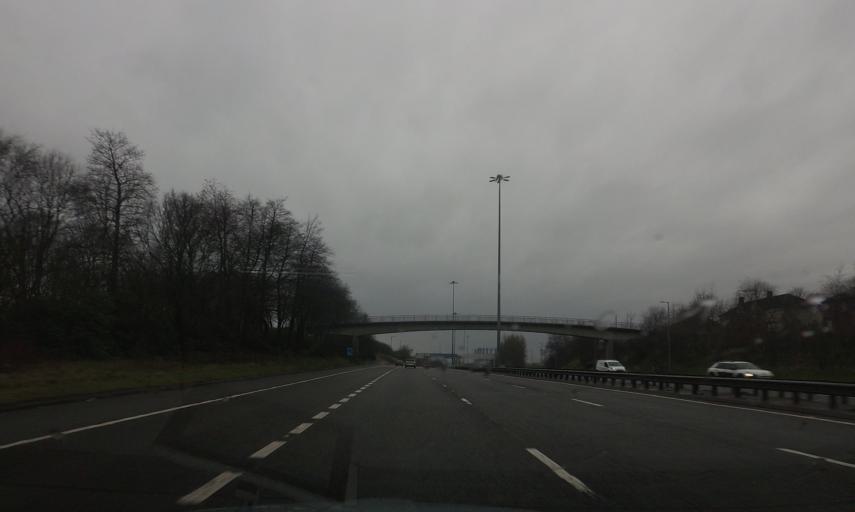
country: GB
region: Scotland
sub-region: North Lanarkshire
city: Stepps
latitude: 55.8729
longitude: -4.1911
